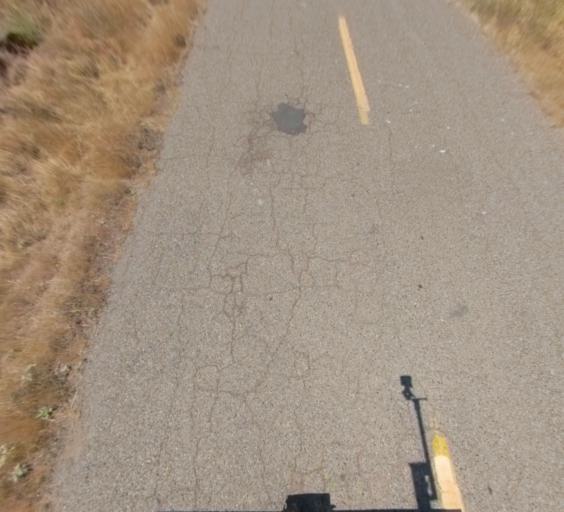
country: US
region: California
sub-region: Madera County
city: Madera Acres
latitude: 37.0838
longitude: -120.0153
